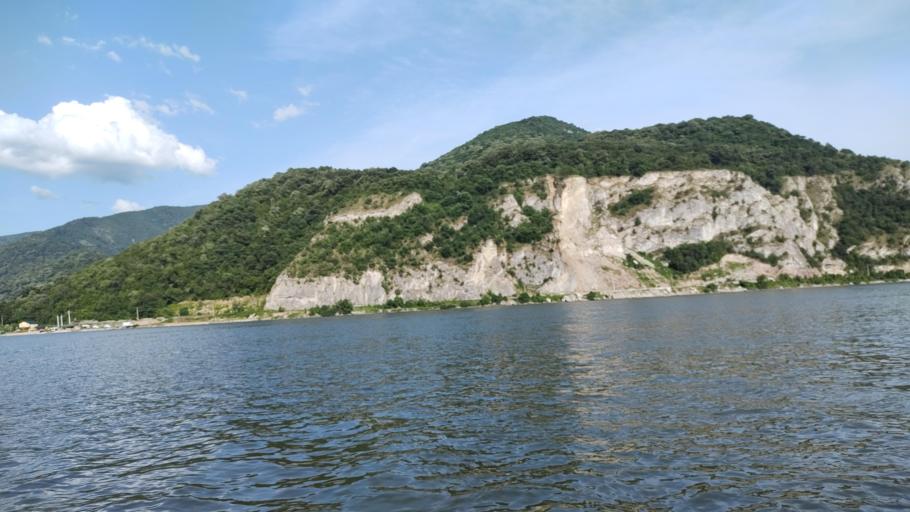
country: RO
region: Caras-Severin
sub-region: Comuna Berzasca
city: Berzasca
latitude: 44.6164
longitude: 22.0014
